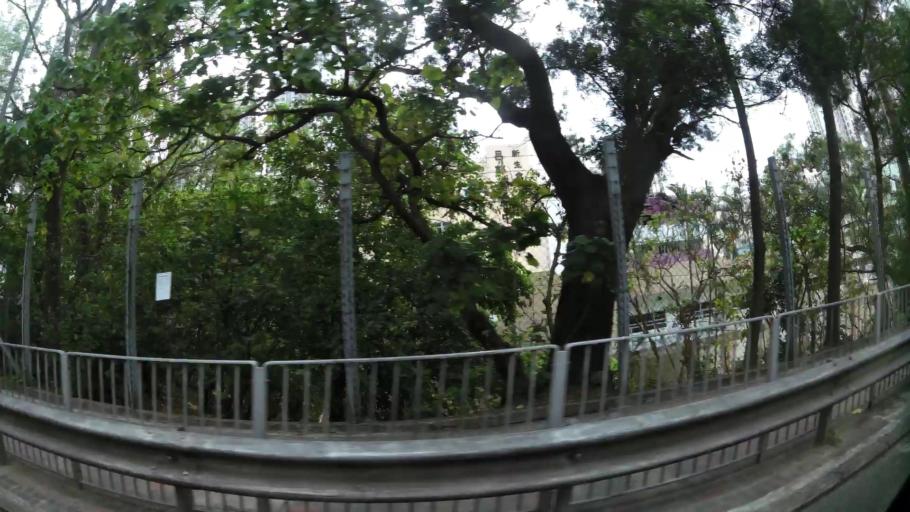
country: HK
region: Kowloon City
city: Kowloon
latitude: 22.3192
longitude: 114.2276
